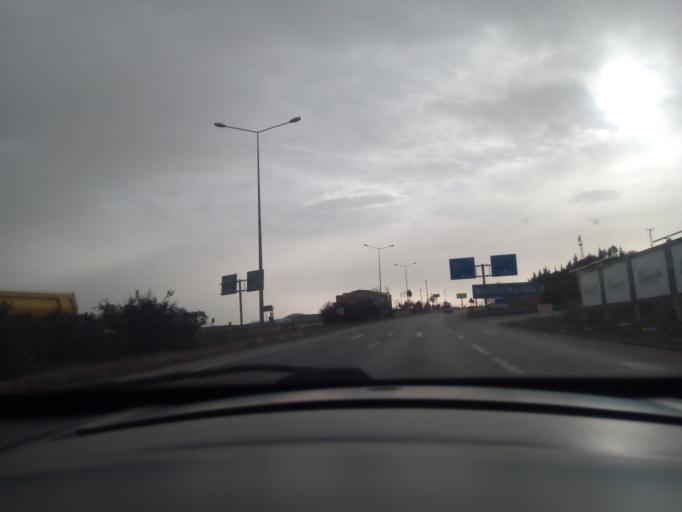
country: TR
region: Bursa
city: Tatkavakli
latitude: 40.0501
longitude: 28.3708
